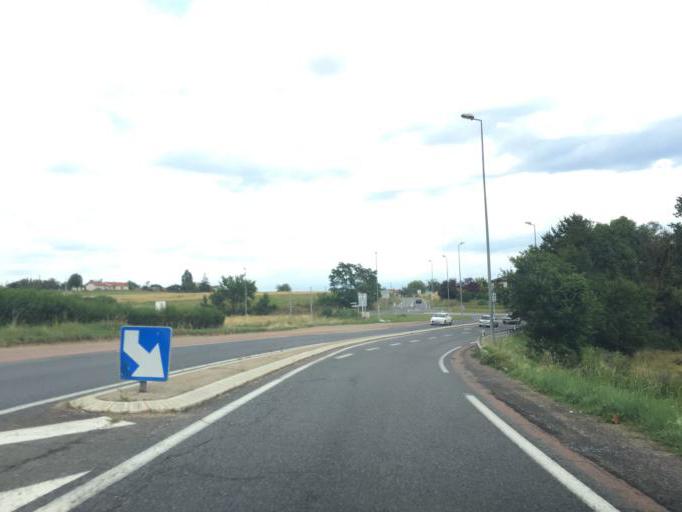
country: FR
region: Rhone-Alpes
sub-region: Departement du Rhone
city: Pontcharra-sur-Turdine
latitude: 45.8779
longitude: 4.5119
